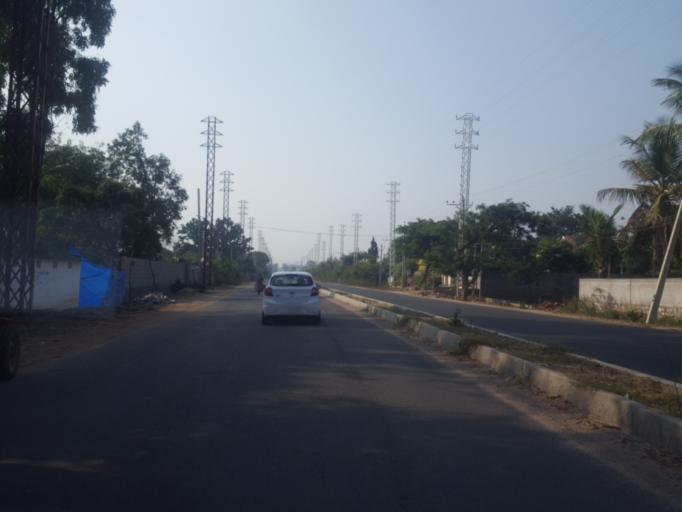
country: IN
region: Telangana
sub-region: Medak
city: Serilingampalle
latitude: 17.3998
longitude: 78.2970
